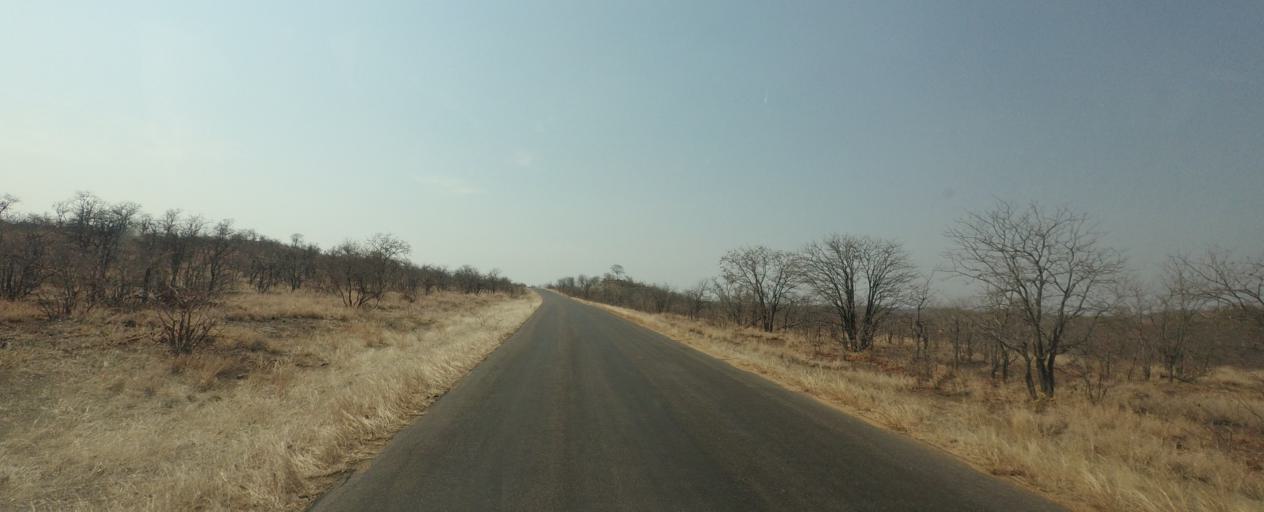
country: ZA
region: Limpopo
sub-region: Mopani District Municipality
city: Phalaborwa
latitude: -23.9959
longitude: 31.6437
